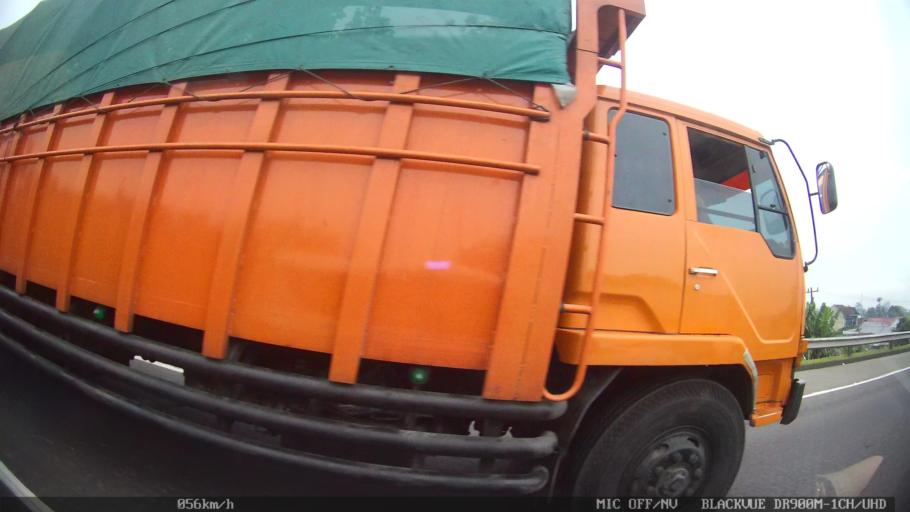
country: ID
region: North Sumatra
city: Medan
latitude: 3.5752
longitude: 98.7252
